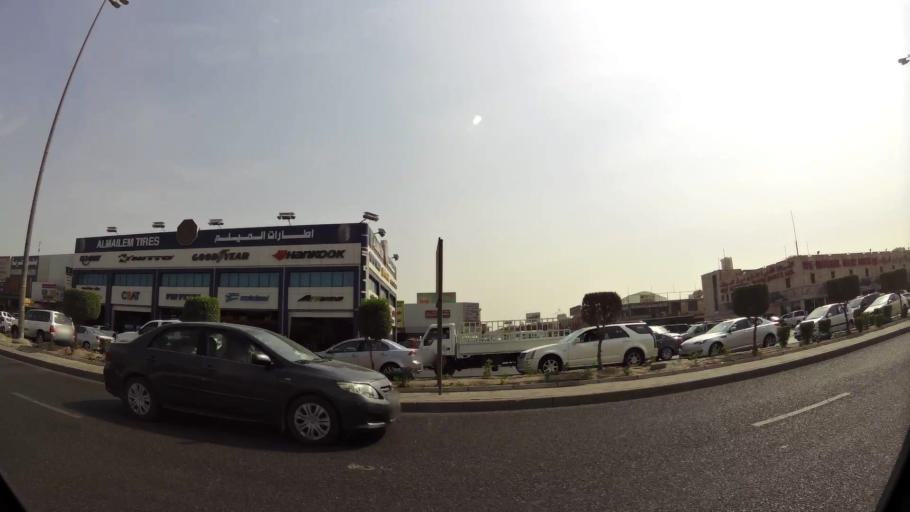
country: KW
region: Al Asimah
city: Ash Shamiyah
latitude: 29.3278
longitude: 47.9429
